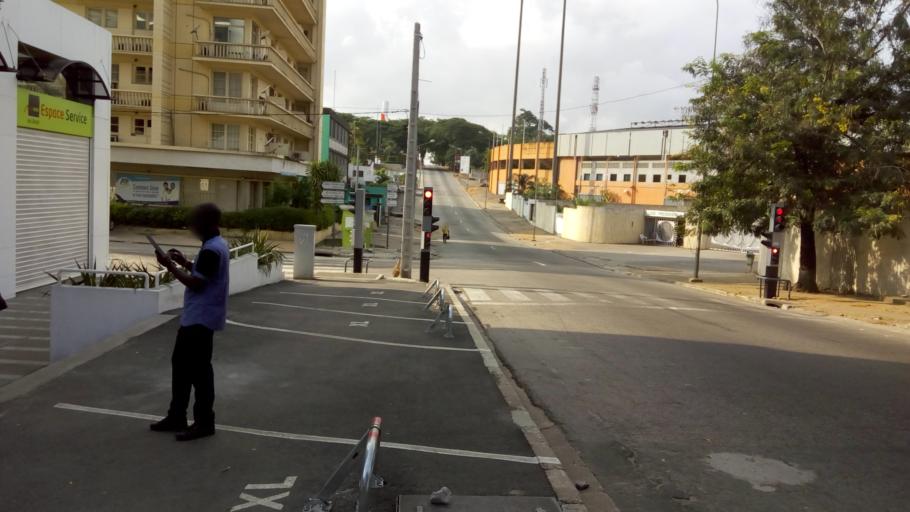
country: CI
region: Lagunes
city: Abidjan
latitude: 5.3272
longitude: -4.0197
